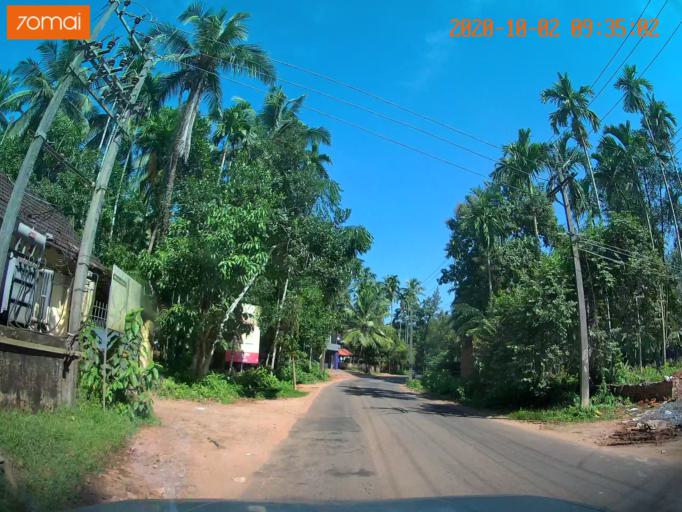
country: IN
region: Kerala
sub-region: Kozhikode
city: Nadapuram
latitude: 11.6419
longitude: 75.7548
